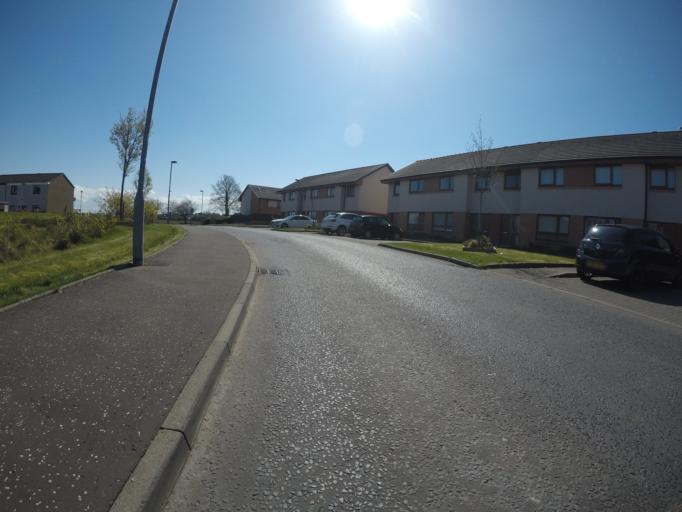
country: GB
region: Scotland
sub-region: North Ayrshire
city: Irvine
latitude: 55.6210
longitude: -4.6656
